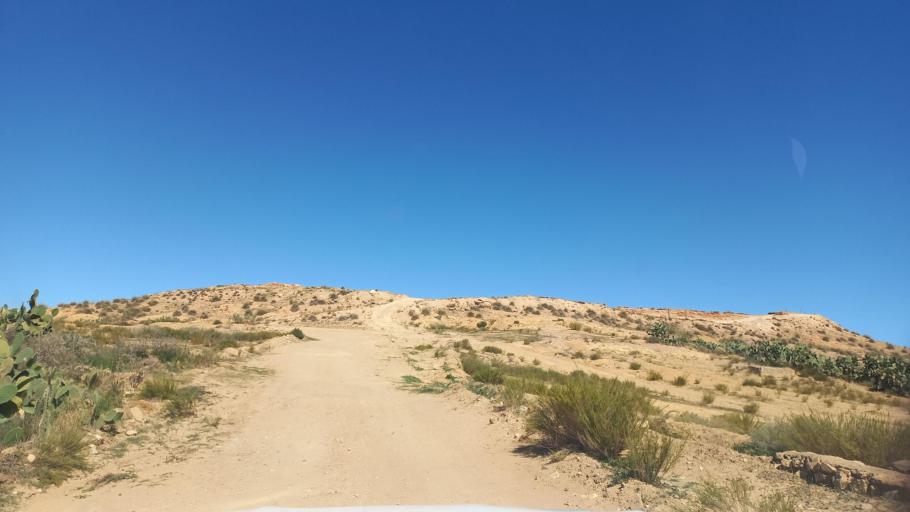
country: TN
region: Al Qasrayn
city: Sbiba
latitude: 35.3558
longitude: 9.1124
